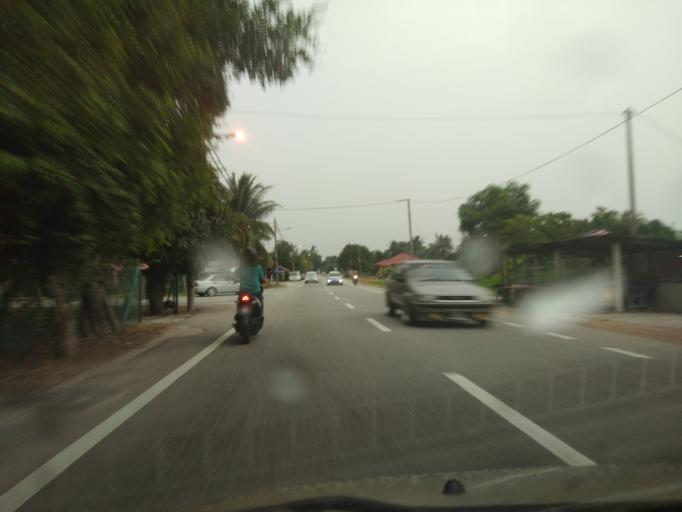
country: MY
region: Penang
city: Permatang Kuching
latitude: 5.4879
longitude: 100.4002
